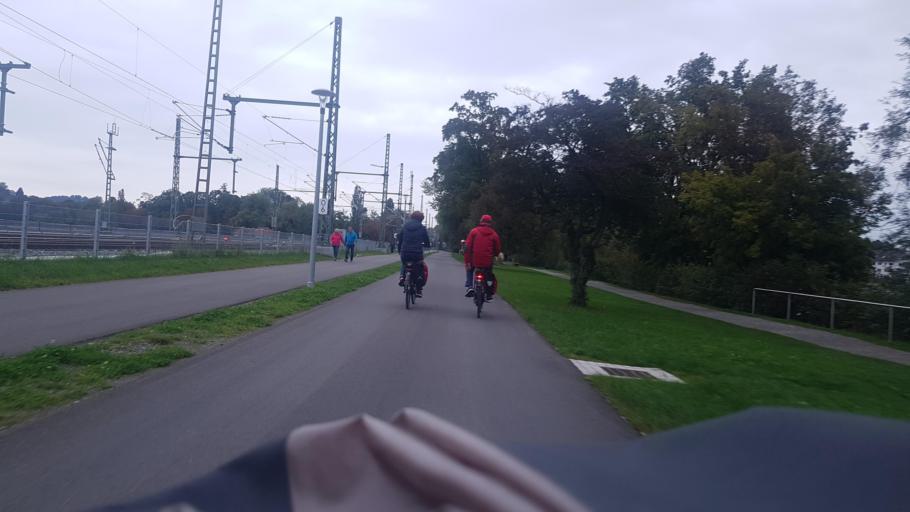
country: DE
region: Bavaria
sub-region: Swabia
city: Lindau
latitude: 47.5497
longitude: 9.6818
